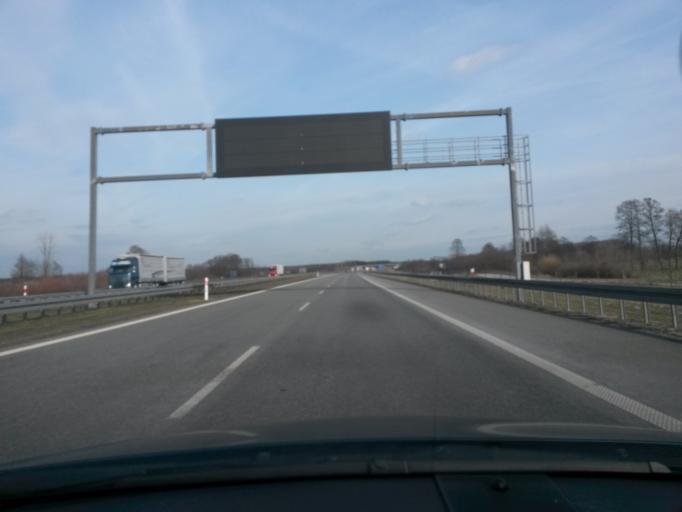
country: PL
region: Greater Poland Voivodeship
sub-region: Powiat koninski
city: Stare Miasto
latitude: 52.1602
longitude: 18.2406
